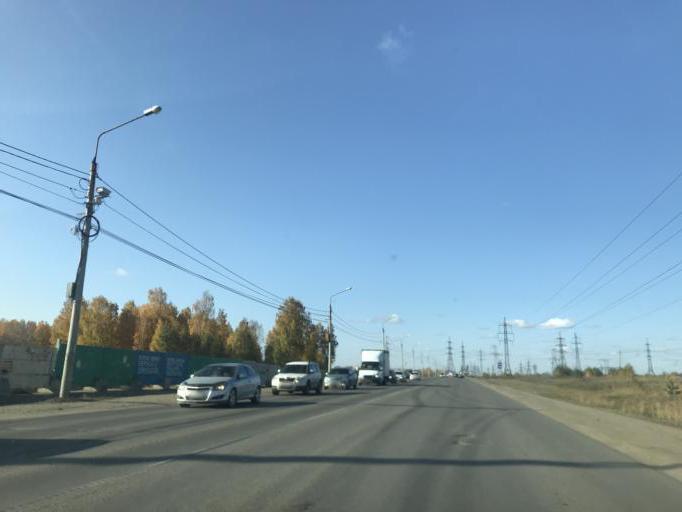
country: RU
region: Chelyabinsk
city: Roshchino
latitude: 55.2208
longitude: 61.2964
